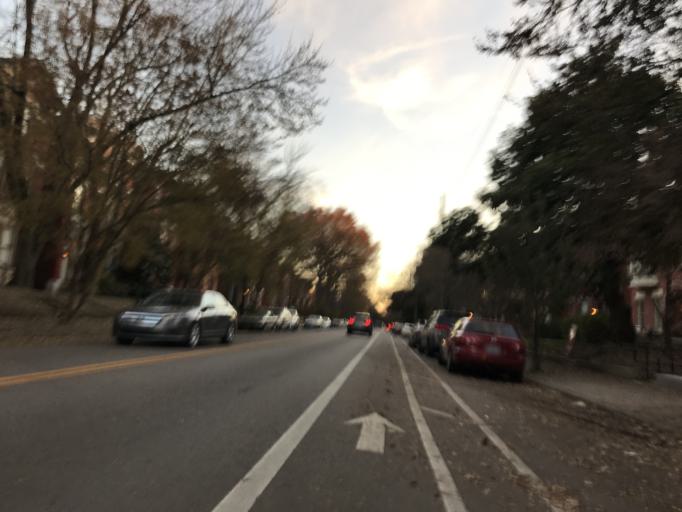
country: US
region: Kentucky
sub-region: Jefferson County
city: Louisville
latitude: 38.2344
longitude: -85.7554
